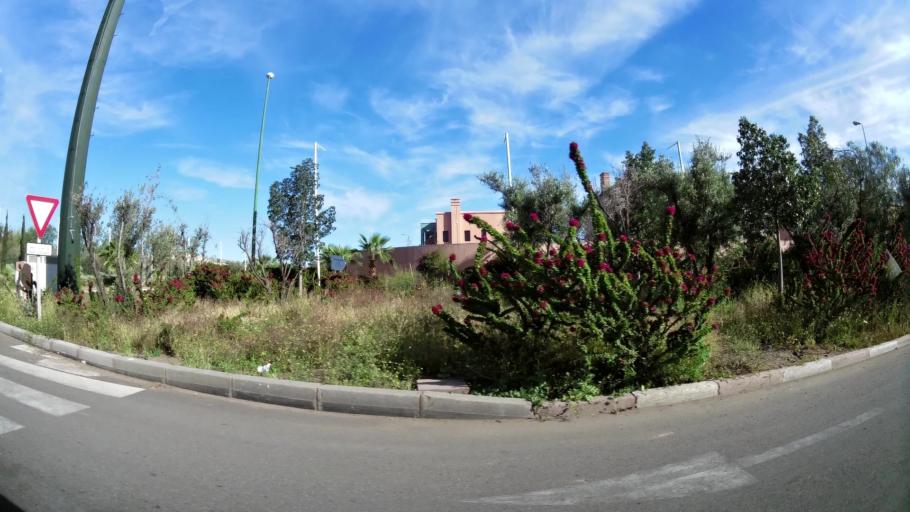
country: MA
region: Marrakech-Tensift-Al Haouz
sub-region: Marrakech
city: Marrakesh
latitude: 31.6791
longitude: -8.0538
